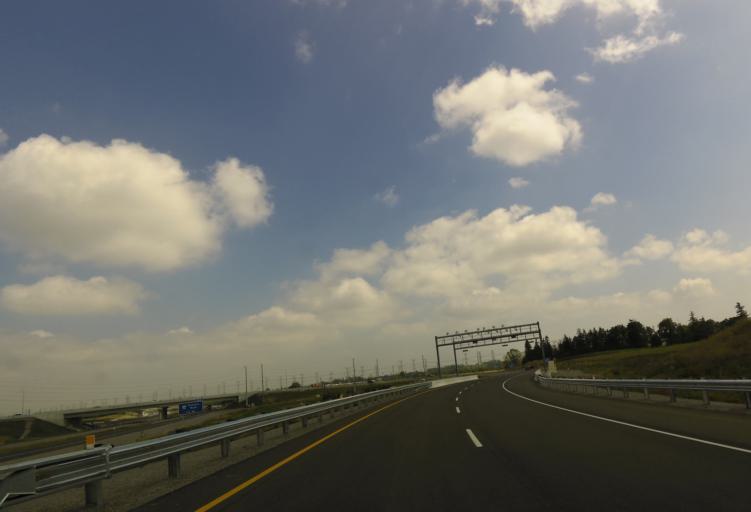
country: CA
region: Ontario
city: Ajax
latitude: 43.9473
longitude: -78.9641
